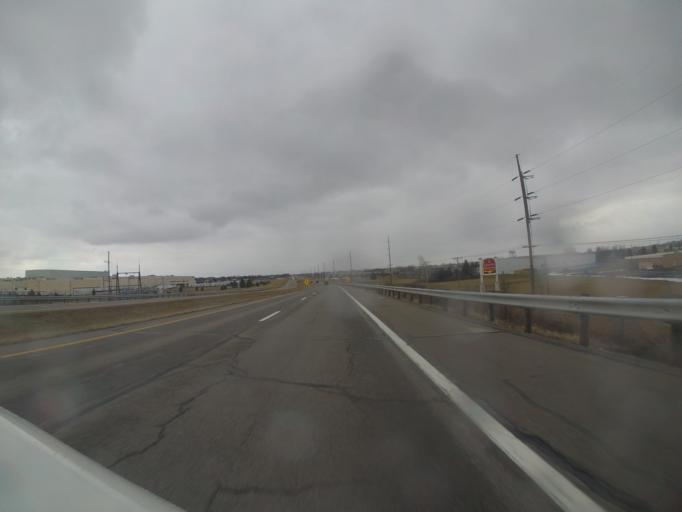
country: US
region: Ohio
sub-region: Wood County
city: Rossford
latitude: 41.5639
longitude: -83.5497
